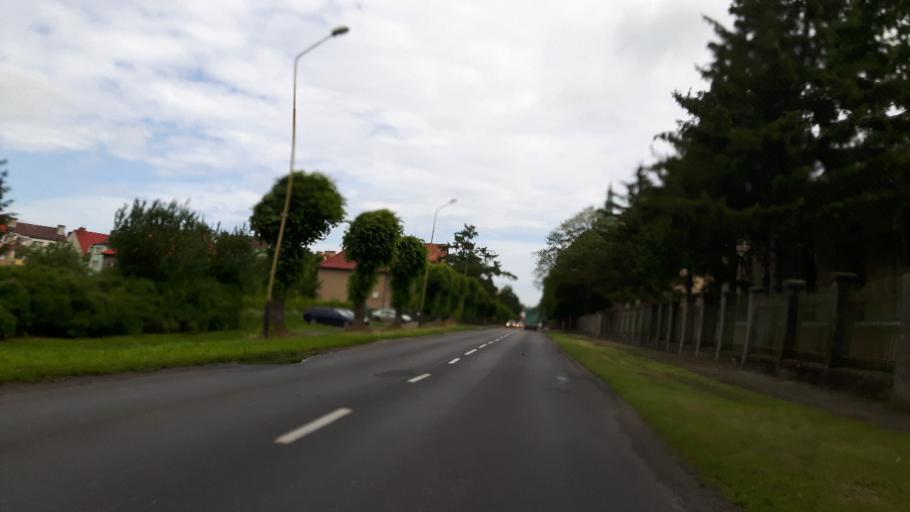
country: PL
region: West Pomeranian Voivodeship
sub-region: Powiat gryficki
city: Trzebiatow
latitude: 54.0524
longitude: 15.2566
